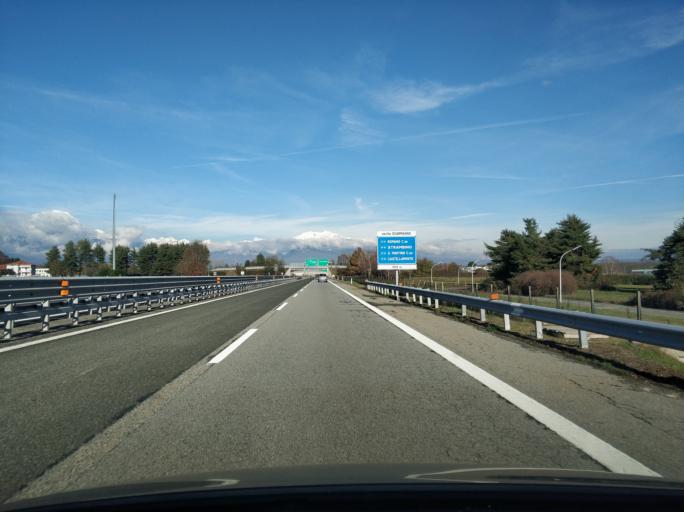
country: IT
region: Piedmont
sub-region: Provincia di Torino
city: Scarmagno
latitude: 45.3828
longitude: 7.8461
